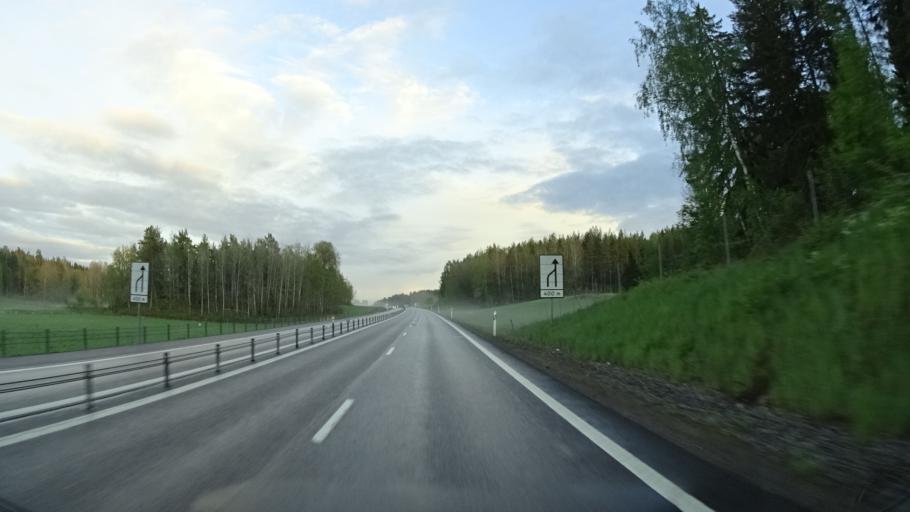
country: SE
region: OEstergoetland
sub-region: Valdemarsviks Kommun
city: Gusum
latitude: 58.3731
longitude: 16.4259
